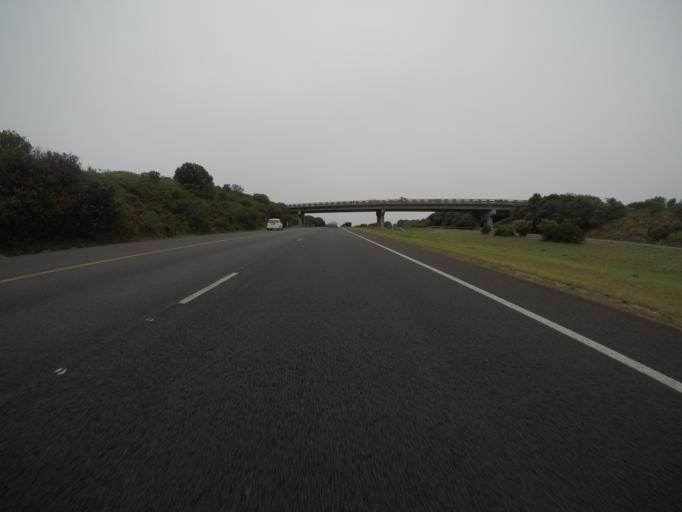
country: ZA
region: Western Cape
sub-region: Eden District Municipality
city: Mossel Bay
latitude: -34.0613
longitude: 22.1880
